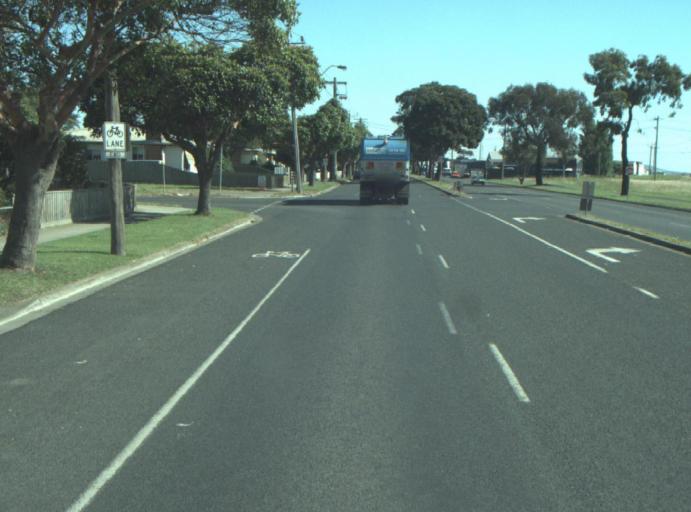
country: AU
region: Victoria
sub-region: Greater Geelong
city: Bell Park
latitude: -38.0968
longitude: 144.3651
